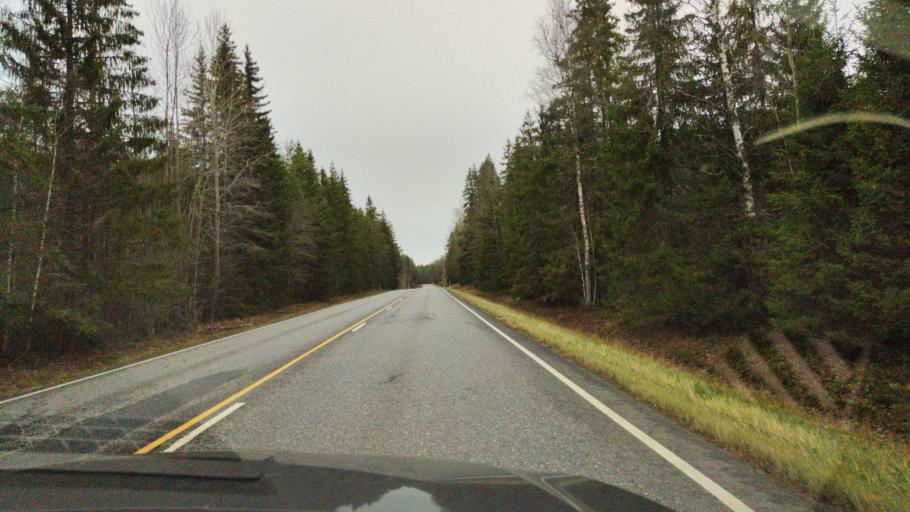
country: FI
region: Varsinais-Suomi
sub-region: Loimaa
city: Ylaene
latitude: 60.7309
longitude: 22.4376
